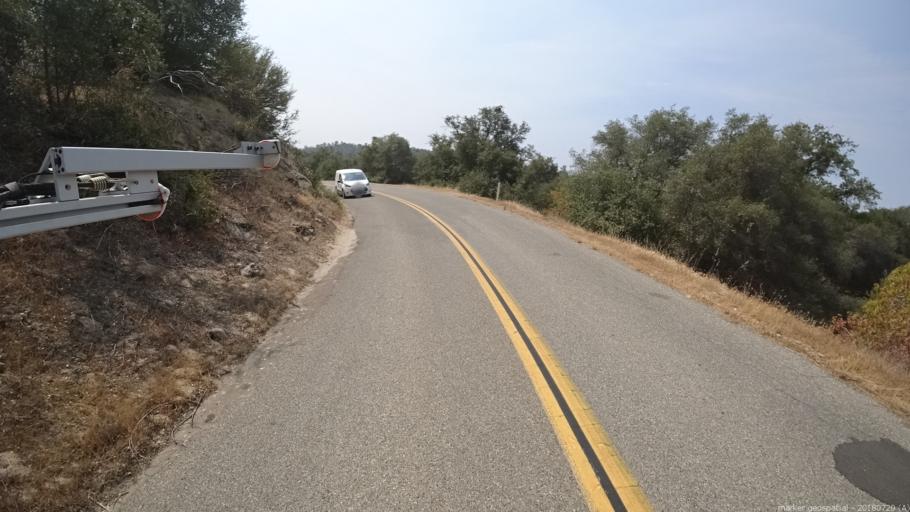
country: US
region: California
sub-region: Madera County
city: Ahwahnee
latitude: 37.3059
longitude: -119.7922
